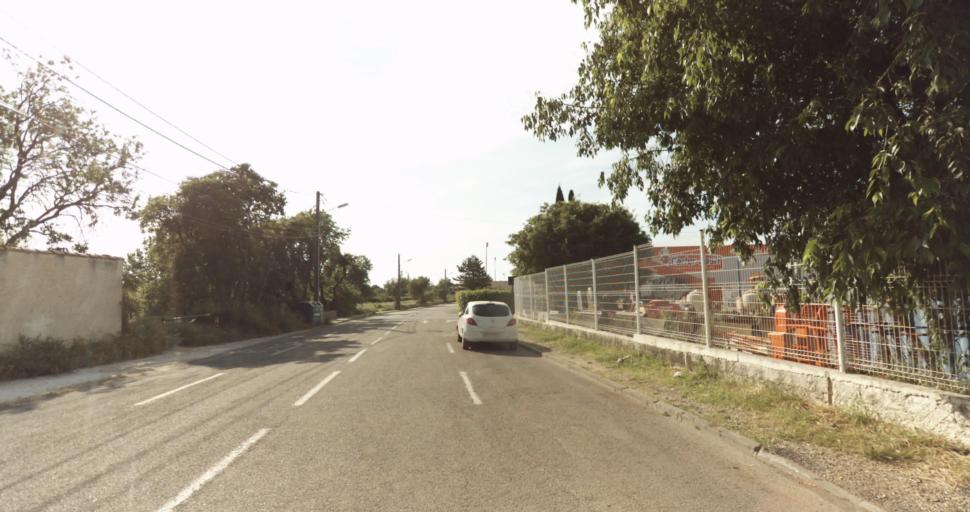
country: FR
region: Languedoc-Roussillon
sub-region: Departement du Gard
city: Rodilhan
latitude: 43.8534
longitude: 4.4022
